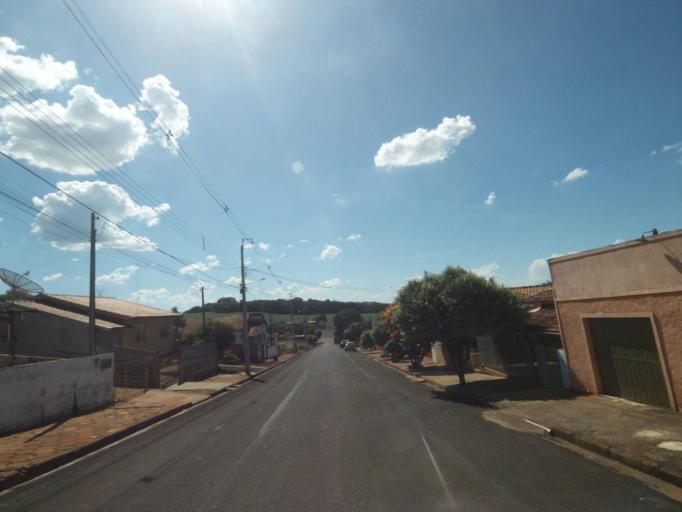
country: BR
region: Parana
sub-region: Sertanopolis
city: Sertanopolis
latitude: -23.0397
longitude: -50.8197
